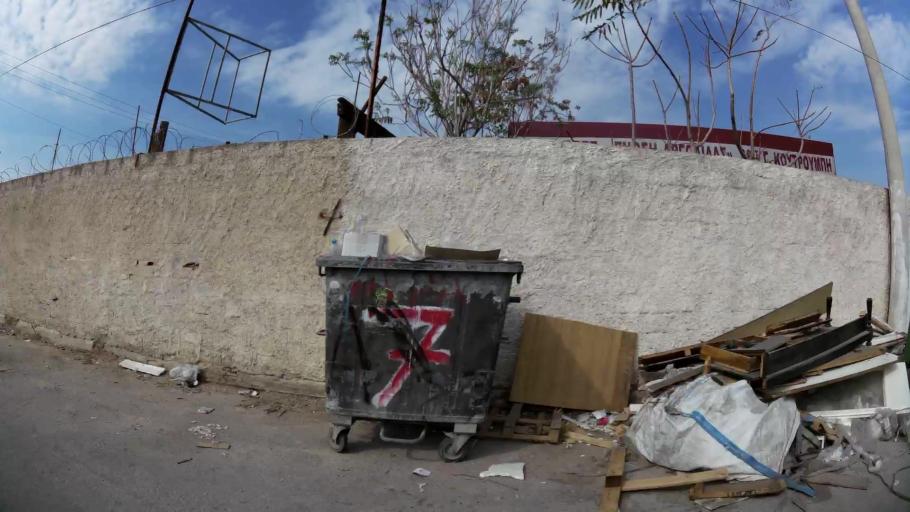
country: GR
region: Attica
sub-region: Nomarchia Athinas
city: Aigaleo
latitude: 37.9915
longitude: 23.6931
